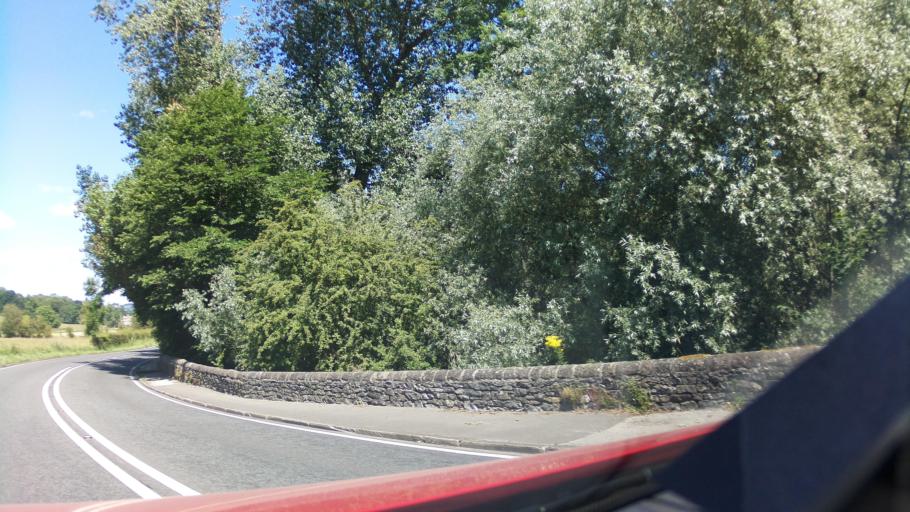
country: GB
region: England
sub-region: Derbyshire
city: Bakewell
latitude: 53.1953
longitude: -1.6580
